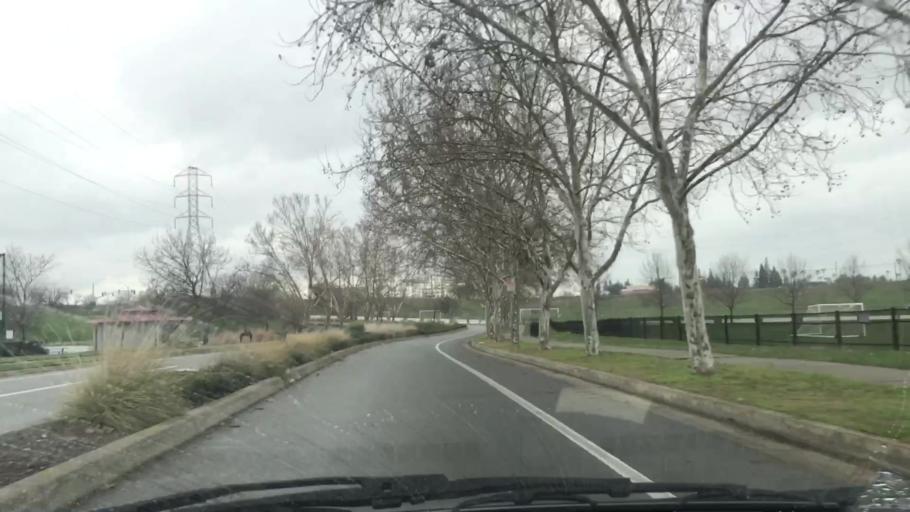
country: US
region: California
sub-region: Sacramento County
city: Rosemont
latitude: 38.5434
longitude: -121.4044
